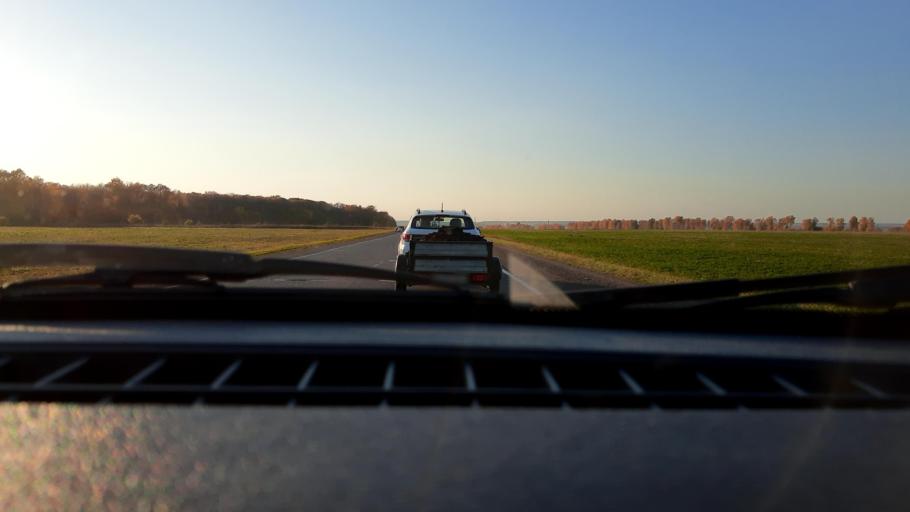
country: RU
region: Bashkortostan
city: Avdon
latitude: 54.8245
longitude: 55.6501
